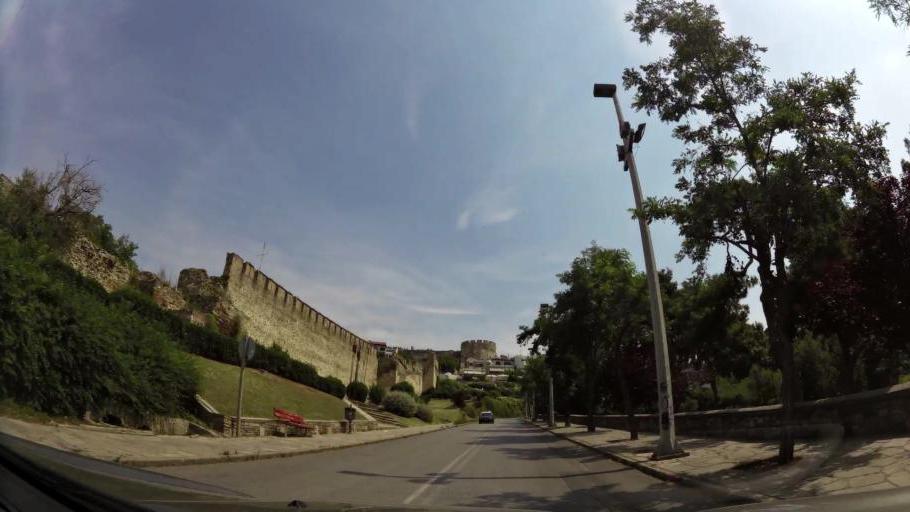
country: GR
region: Central Macedonia
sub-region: Nomos Thessalonikis
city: Agios Pavlos
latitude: 40.6385
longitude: 22.9584
